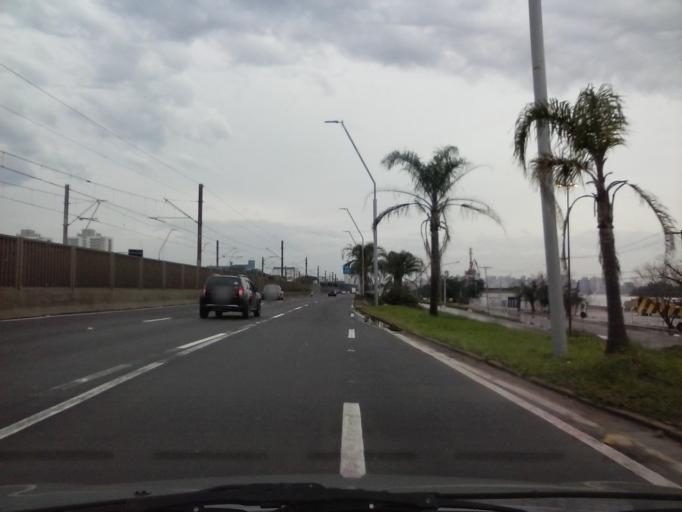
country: BR
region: Rio Grande do Sul
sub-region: Porto Alegre
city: Porto Alegre
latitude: -30.0017
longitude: -51.2080
